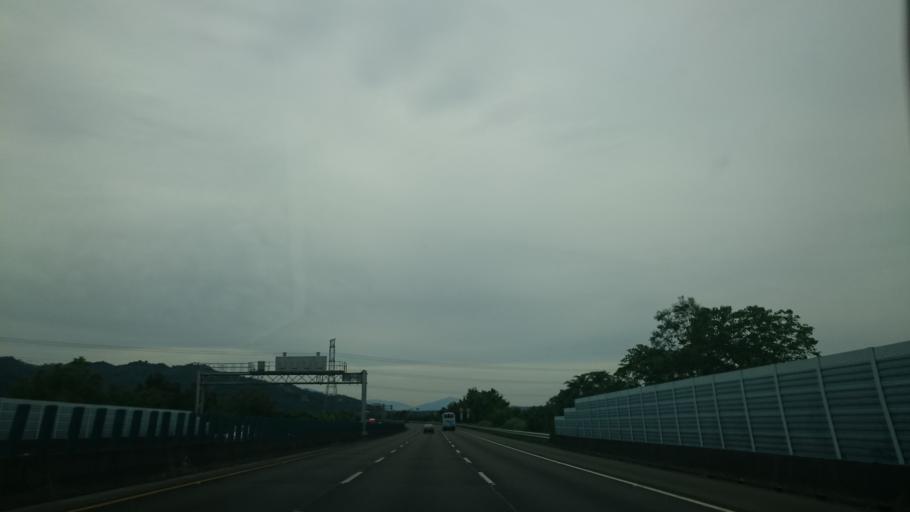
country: TW
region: Taiwan
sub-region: Nantou
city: Nantou
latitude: 23.8913
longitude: 120.7106
